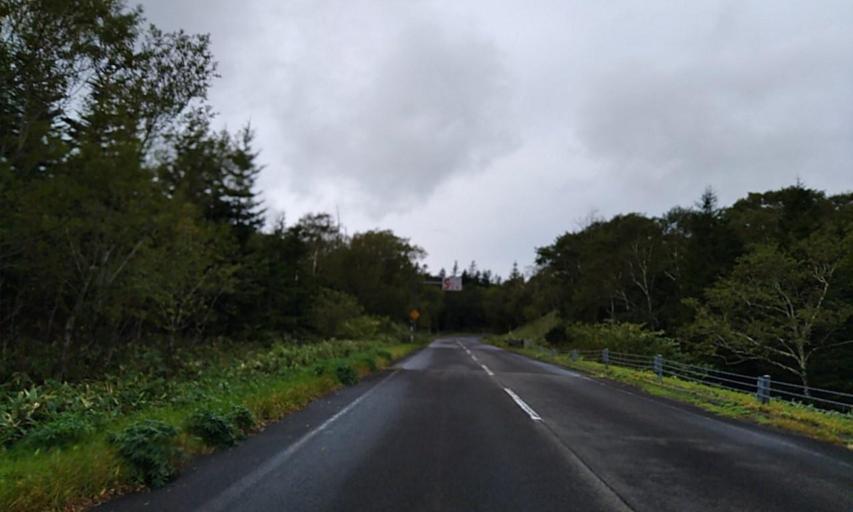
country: JP
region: Hokkaido
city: Abashiri
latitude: 43.6044
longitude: 144.5825
